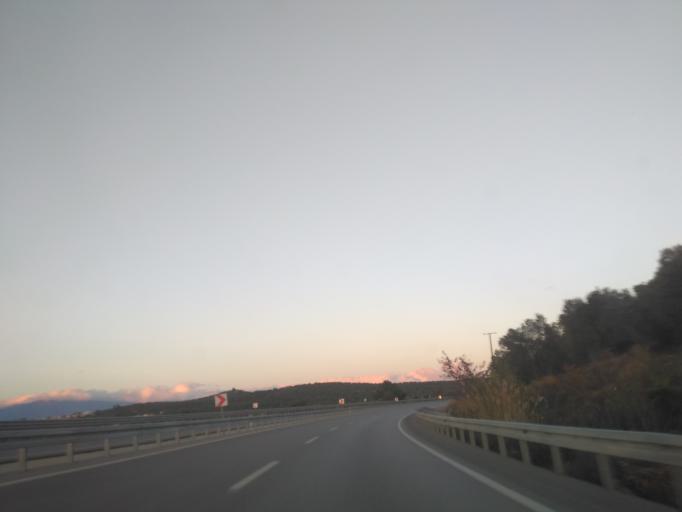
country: TR
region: Balikesir
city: Emrutabat
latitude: 39.4407
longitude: 26.8628
